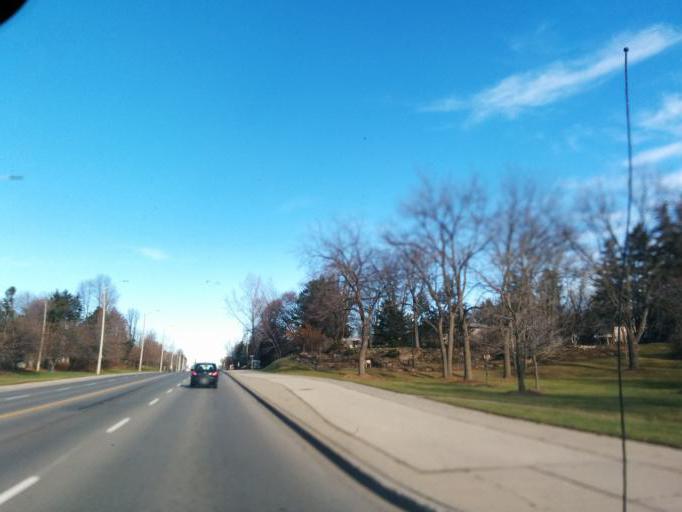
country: CA
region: Ontario
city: Mississauga
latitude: 43.5371
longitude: -79.6015
